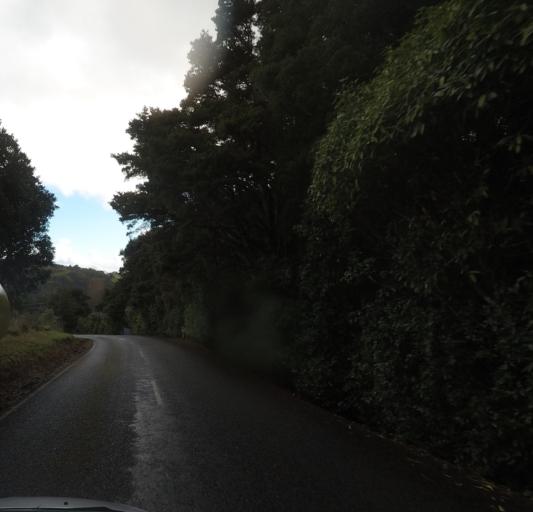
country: NZ
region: Auckland
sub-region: Auckland
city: Warkworth
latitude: -36.3795
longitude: 174.7584
